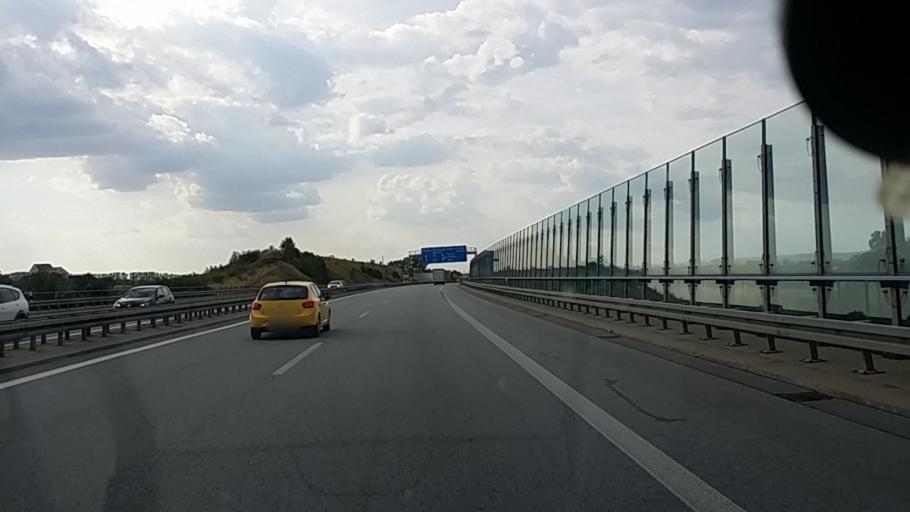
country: DE
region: Saxony
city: Kreischa
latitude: 50.9886
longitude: 13.7747
